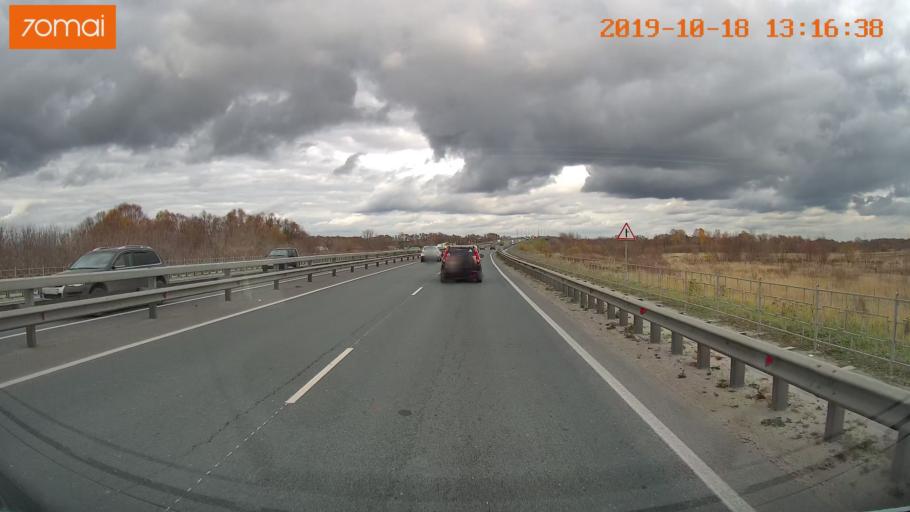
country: RU
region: Rjazan
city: Polyany
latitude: 54.6479
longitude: 39.7925
